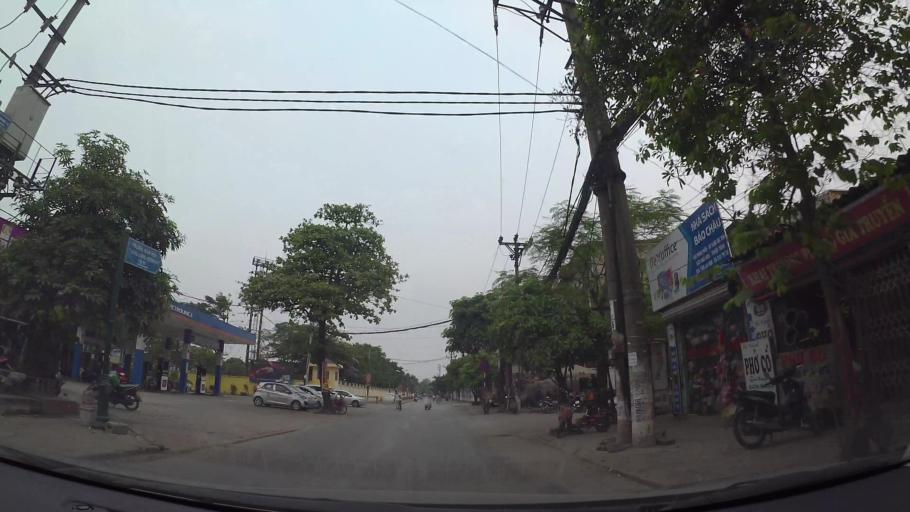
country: VN
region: Ha Noi
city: Hoan Kiem
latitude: 21.0679
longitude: 105.8900
